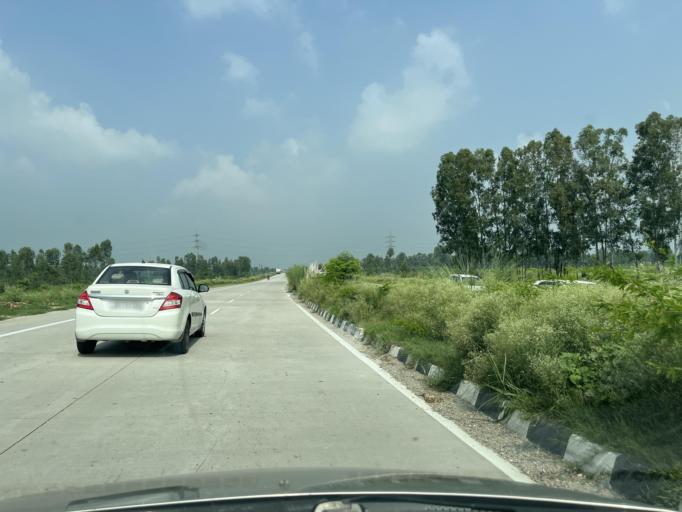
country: IN
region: Uttarakhand
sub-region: Udham Singh Nagar
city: Kashipur
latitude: 29.1644
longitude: 78.9607
